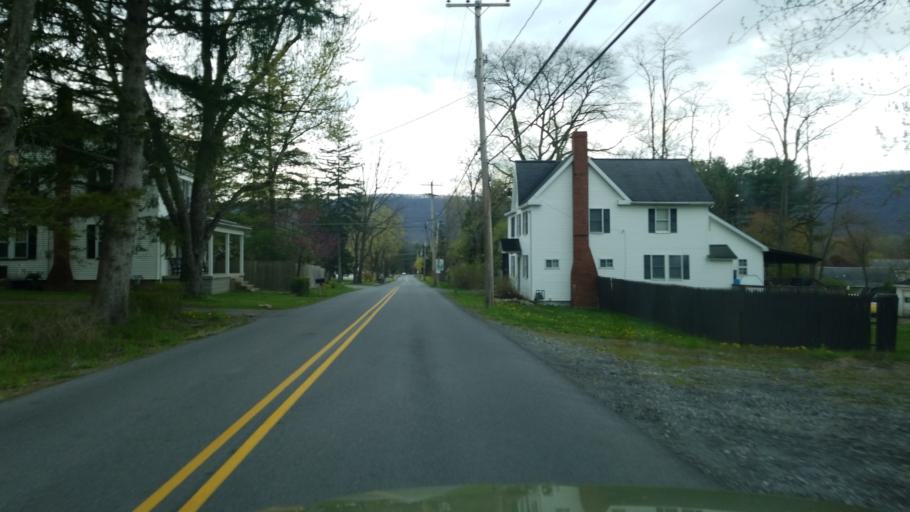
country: US
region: Pennsylvania
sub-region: Blair County
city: Tipton
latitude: 40.6397
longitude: -78.3014
